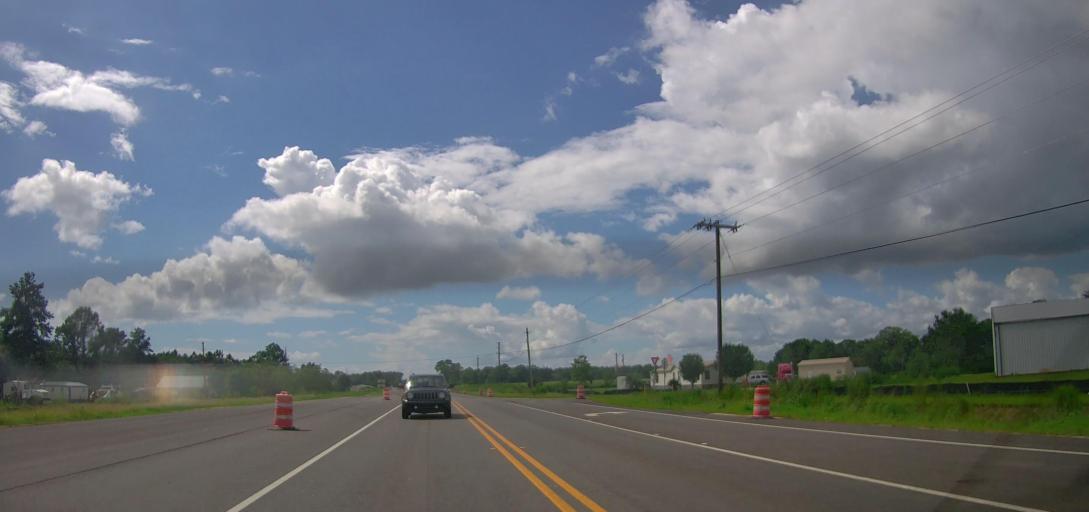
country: US
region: Georgia
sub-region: Coffee County
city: Douglas
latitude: 31.5416
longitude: -82.9278
